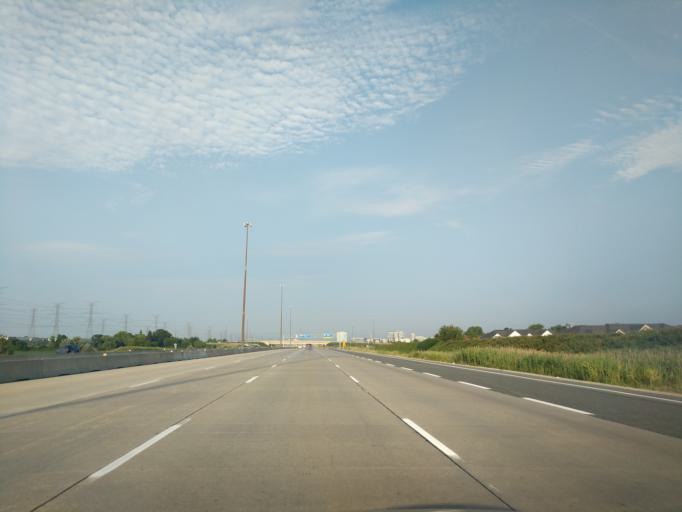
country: CA
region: Ontario
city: Markham
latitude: 43.8525
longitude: -79.2987
